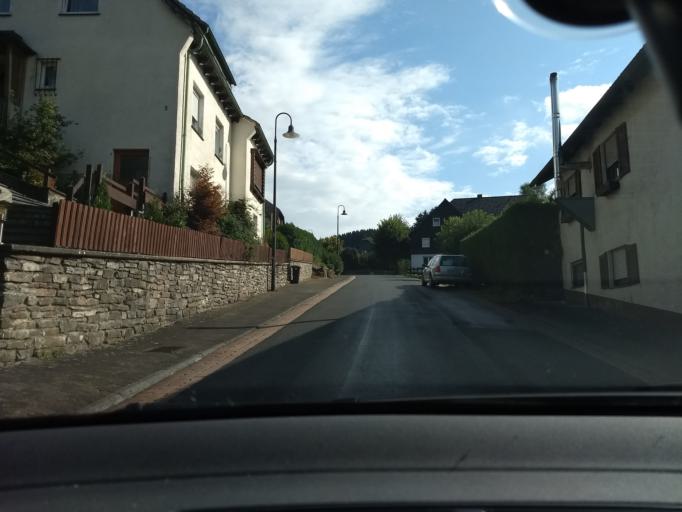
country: DE
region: North Rhine-Westphalia
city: Eslohe
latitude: 51.2508
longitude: 8.1264
